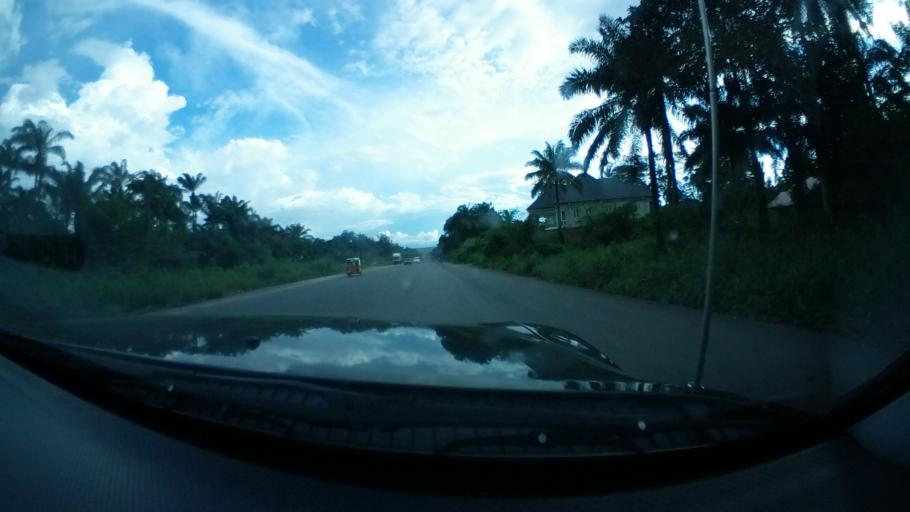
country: NG
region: Imo
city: Orlu
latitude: 5.7222
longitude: 7.0118
